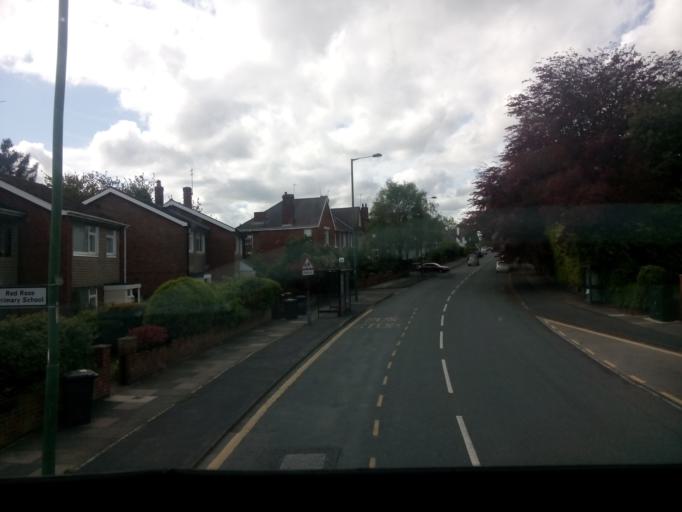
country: GB
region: England
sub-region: County Durham
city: Chester-le-Street
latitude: 54.8493
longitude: -1.5728
